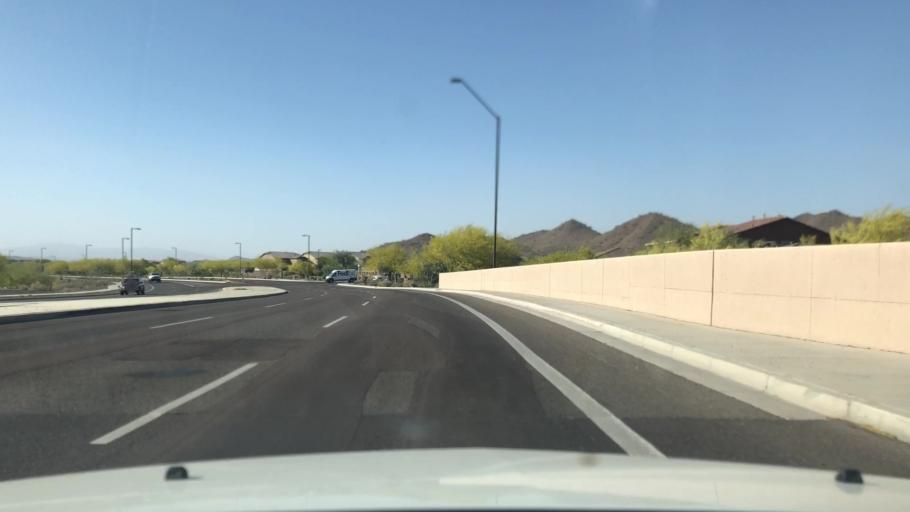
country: US
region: Arizona
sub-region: Maricopa County
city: Anthem
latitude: 33.7297
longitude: -112.0995
